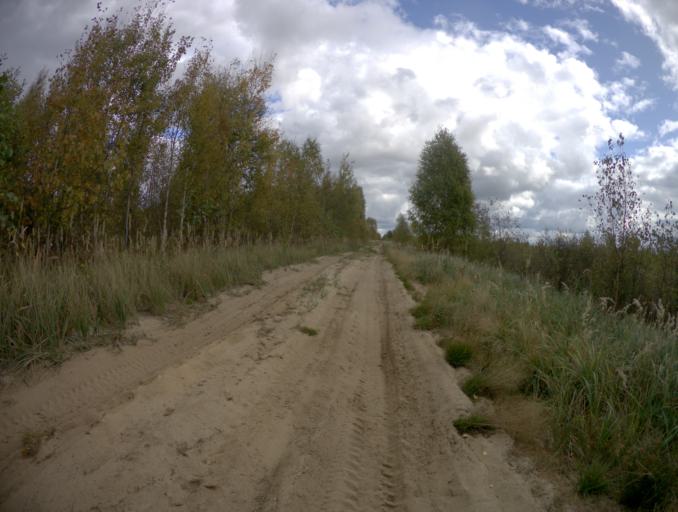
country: RU
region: Vladimir
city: Urshel'skiy
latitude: 55.7684
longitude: 40.1226
